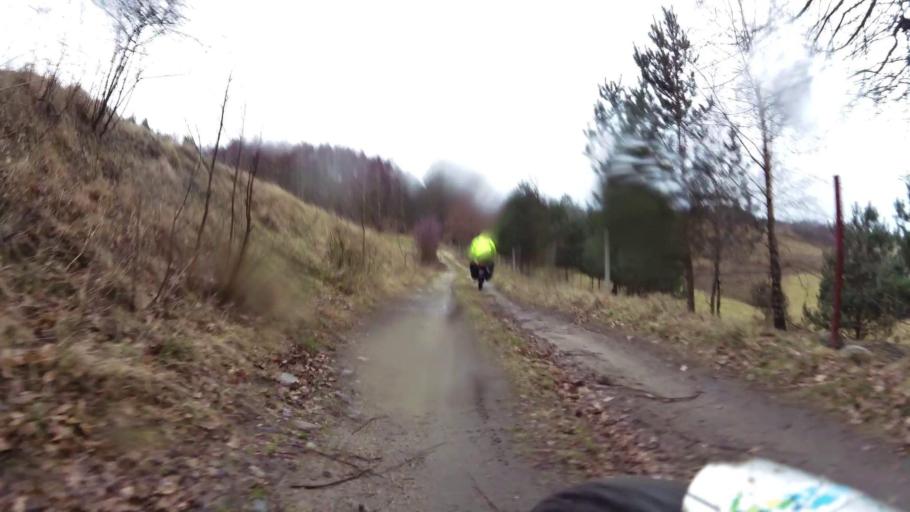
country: PL
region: Pomeranian Voivodeship
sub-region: Powiat bytowski
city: Miastko
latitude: 54.0297
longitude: 17.0220
